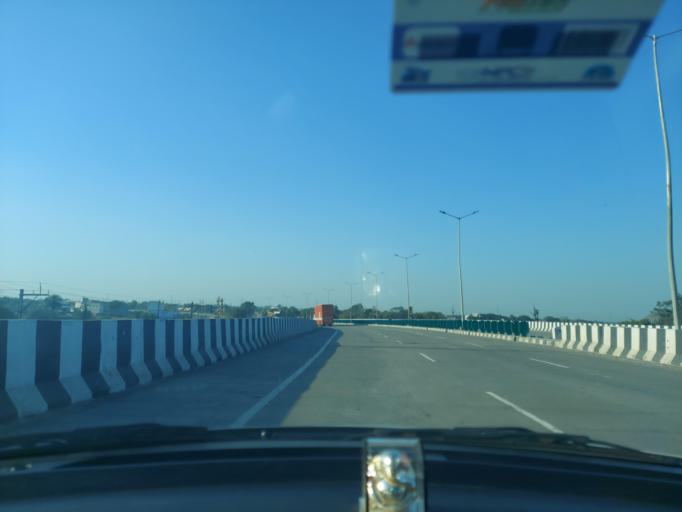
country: IN
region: Madhya Pradesh
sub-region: Dewas
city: Dewas
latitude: 22.9923
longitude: 76.0843
